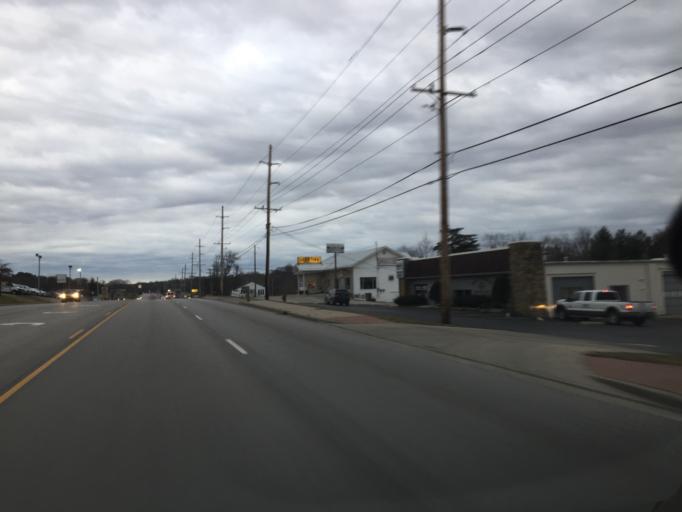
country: US
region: Indiana
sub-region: Monroe County
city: Ellettsville
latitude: 39.2230
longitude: -86.6090
